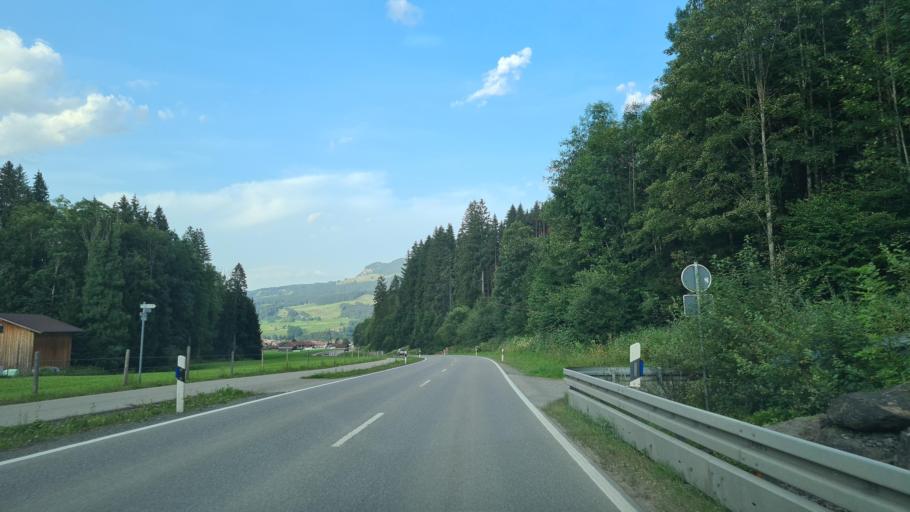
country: DE
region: Bavaria
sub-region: Swabia
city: Obermaiselstein
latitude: 47.4548
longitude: 10.2467
